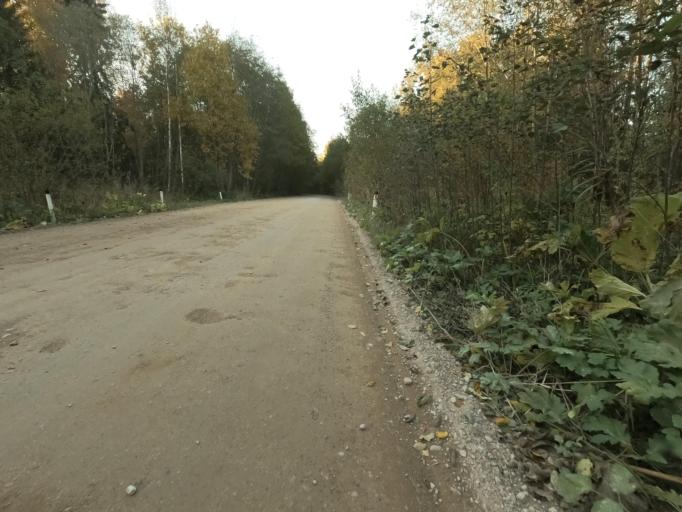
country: RU
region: Leningrad
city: Lyuban'
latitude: 58.9964
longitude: 31.1055
